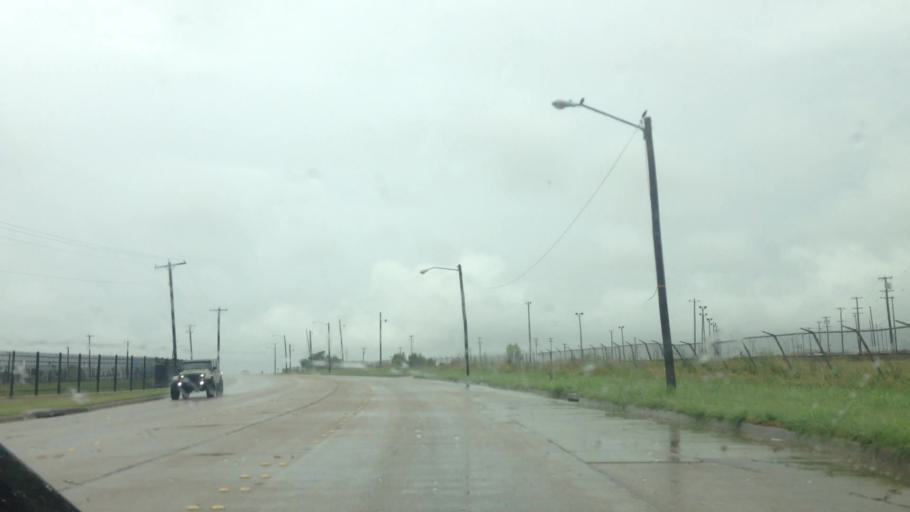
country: US
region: Texas
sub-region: Tarrant County
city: Saginaw
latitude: 32.8297
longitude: -97.3578
